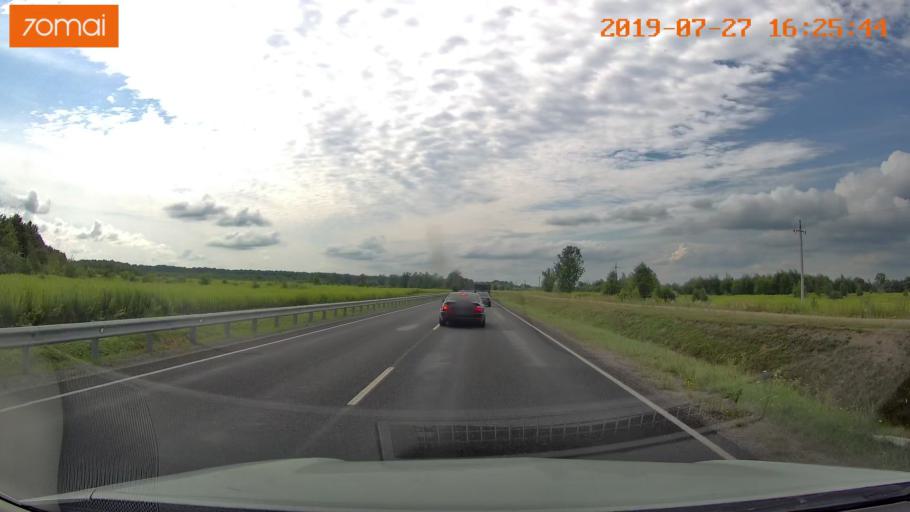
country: RU
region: Kaliningrad
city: Zheleznodorozhnyy
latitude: 54.6381
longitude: 21.4253
